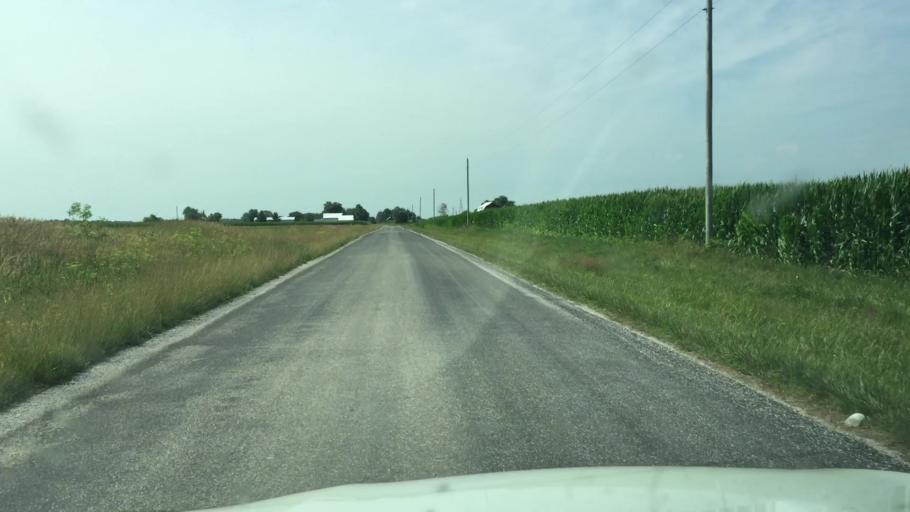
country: US
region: Illinois
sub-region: Hancock County
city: Nauvoo
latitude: 40.5107
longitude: -91.3278
